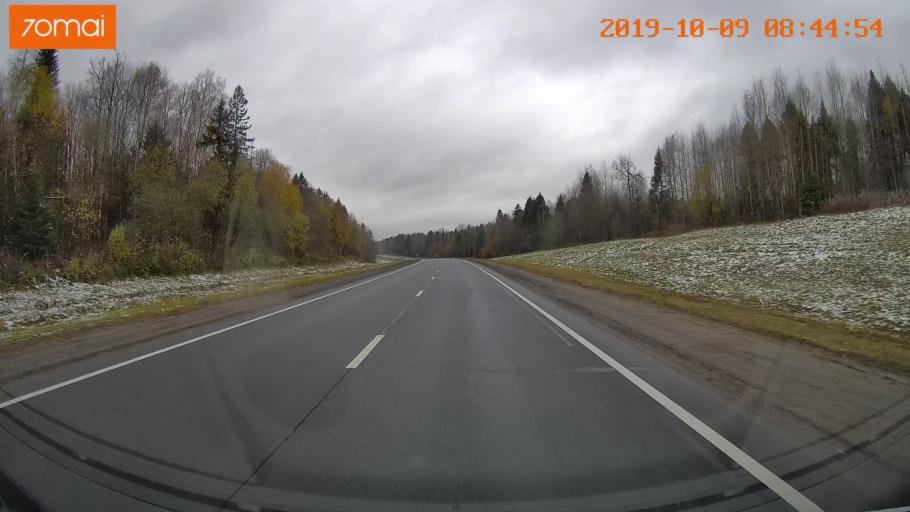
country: RU
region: Vologda
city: Gryazovets
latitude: 59.0424
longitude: 40.1020
